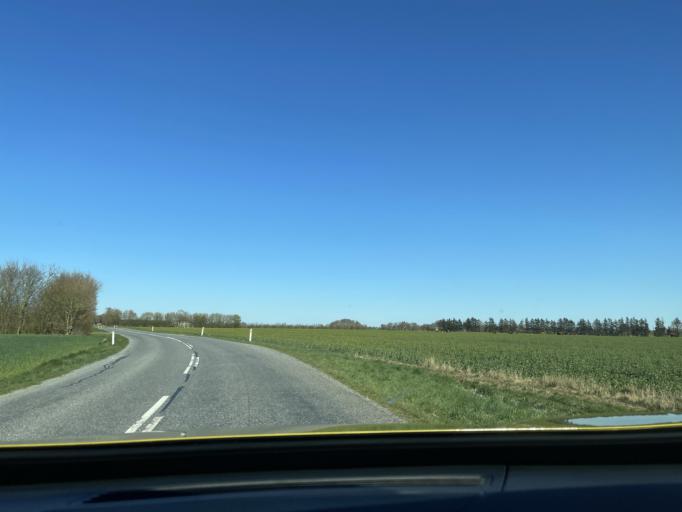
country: DK
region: Central Jutland
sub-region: Silkeborg Kommune
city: Kjellerup
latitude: 56.2529
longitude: 9.3421
